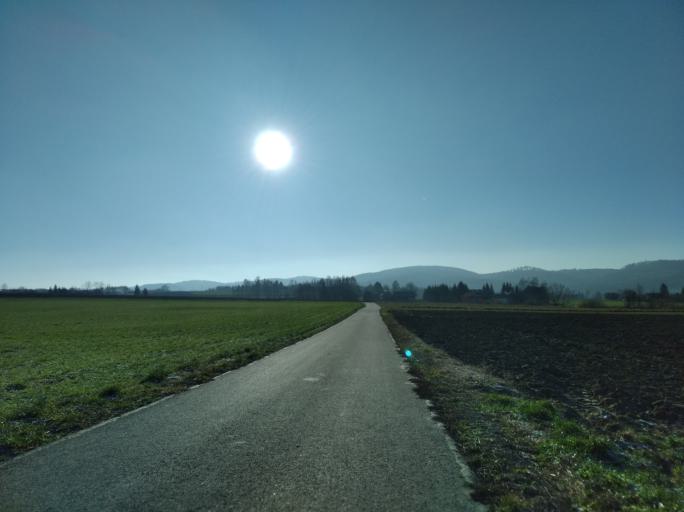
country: PL
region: Subcarpathian Voivodeship
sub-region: Powiat strzyzowski
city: Wysoka Strzyzowska
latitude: 49.8590
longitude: 21.7116
